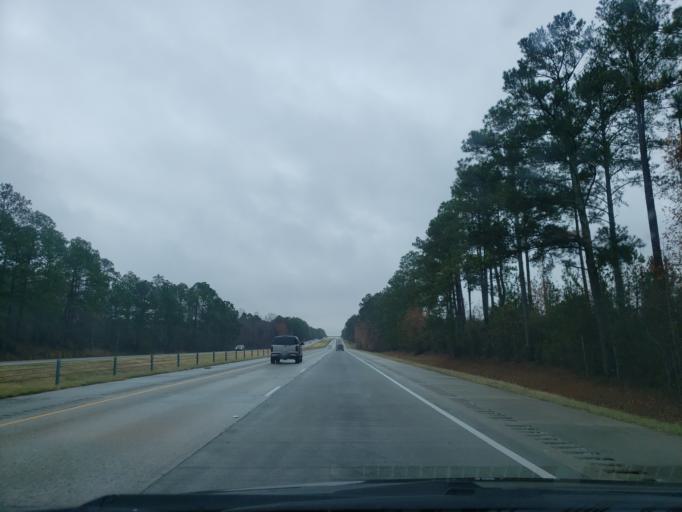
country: US
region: Georgia
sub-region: Laurens County
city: East Dublin
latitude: 32.4485
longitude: -82.7428
